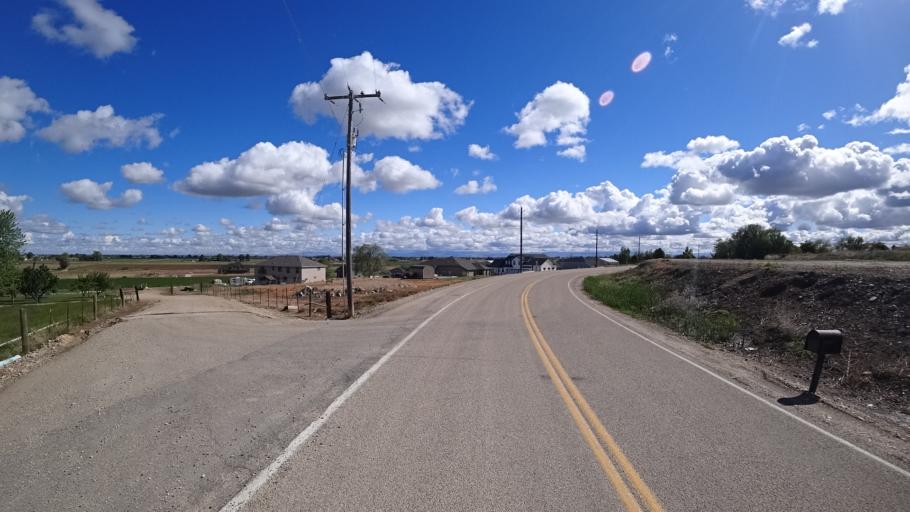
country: US
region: Idaho
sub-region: Ada County
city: Kuna
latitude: 43.4642
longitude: -116.4669
